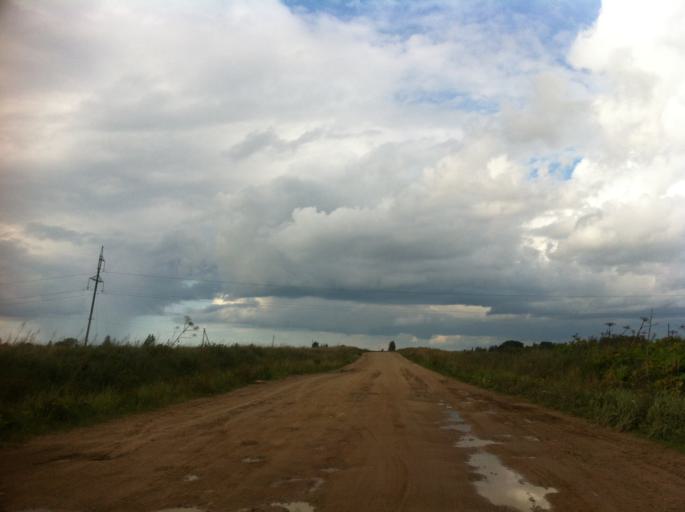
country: RU
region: Pskov
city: Izborsk
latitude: 57.8295
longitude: 27.9825
